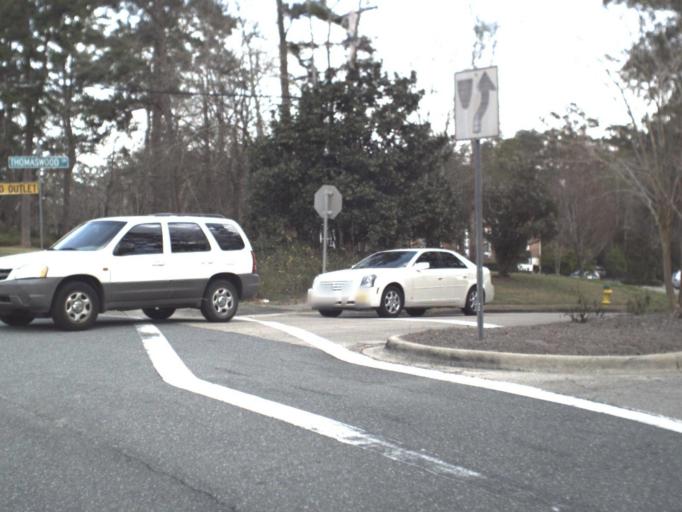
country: US
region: Florida
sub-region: Leon County
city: Tallahassee
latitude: 30.4968
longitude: -84.2540
